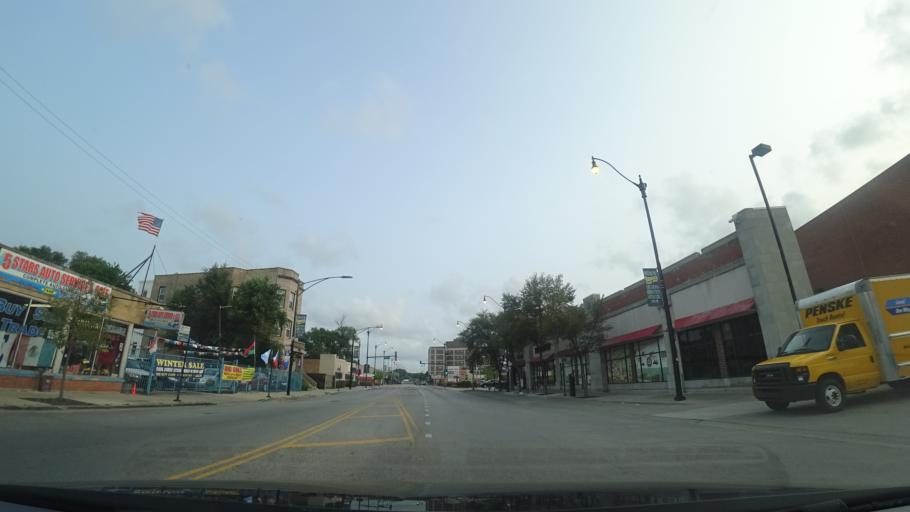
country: US
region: Illinois
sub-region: Cook County
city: Evanston
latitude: 42.0172
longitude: -87.6754
